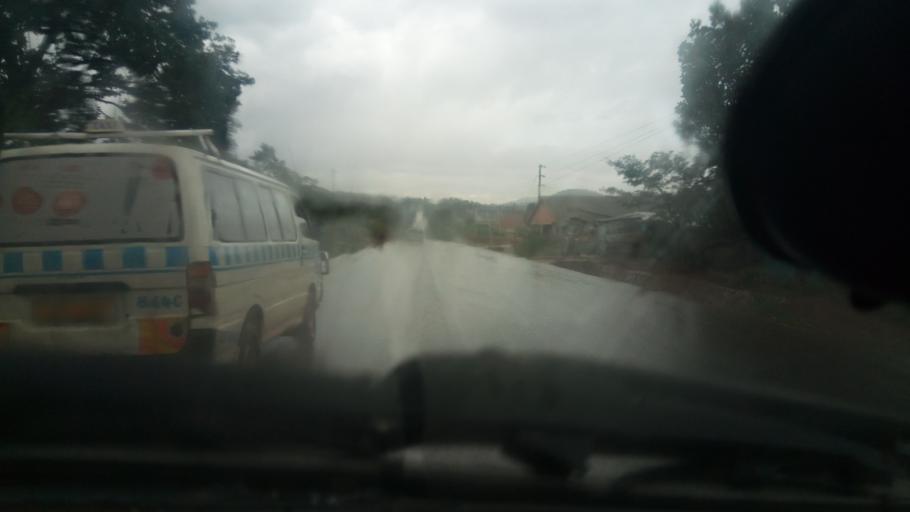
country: UG
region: Central Region
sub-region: Wakiso District
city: Wakiso
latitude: 0.4098
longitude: 32.4639
